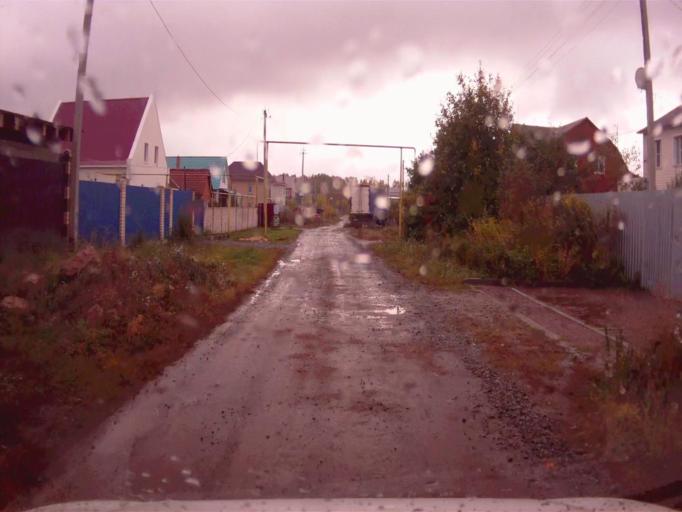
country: RU
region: Chelyabinsk
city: Dolgoderevenskoye
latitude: 55.3047
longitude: 61.3396
